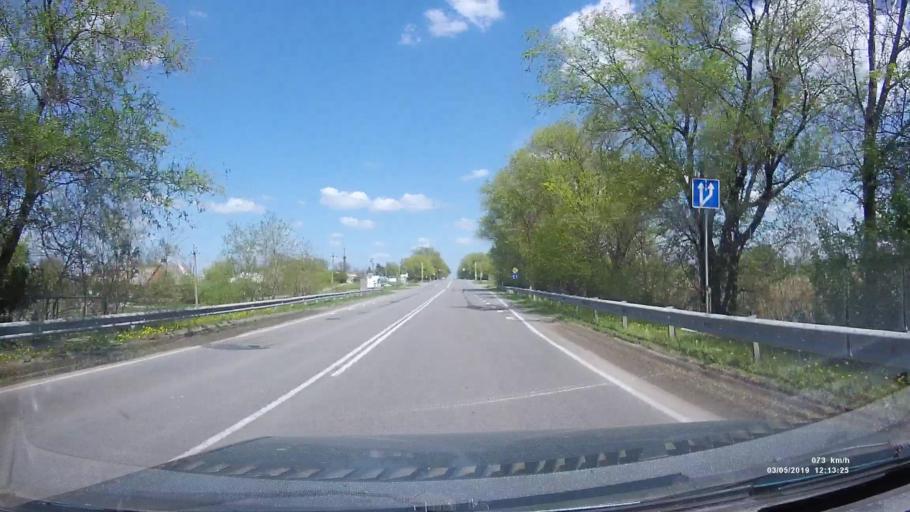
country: RU
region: Rostov
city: Melikhovskaya
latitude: 47.3325
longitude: 40.5548
